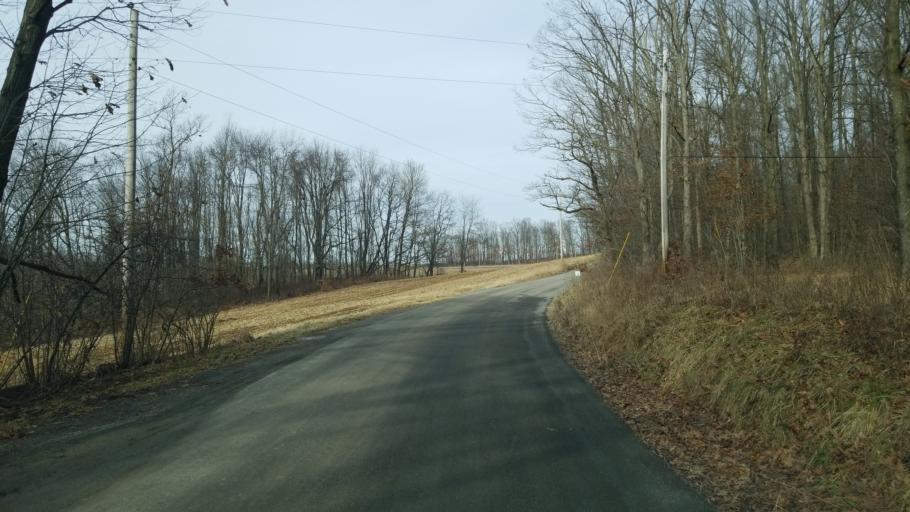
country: US
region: Pennsylvania
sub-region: Jefferson County
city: Punxsutawney
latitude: 40.8766
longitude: -79.0617
